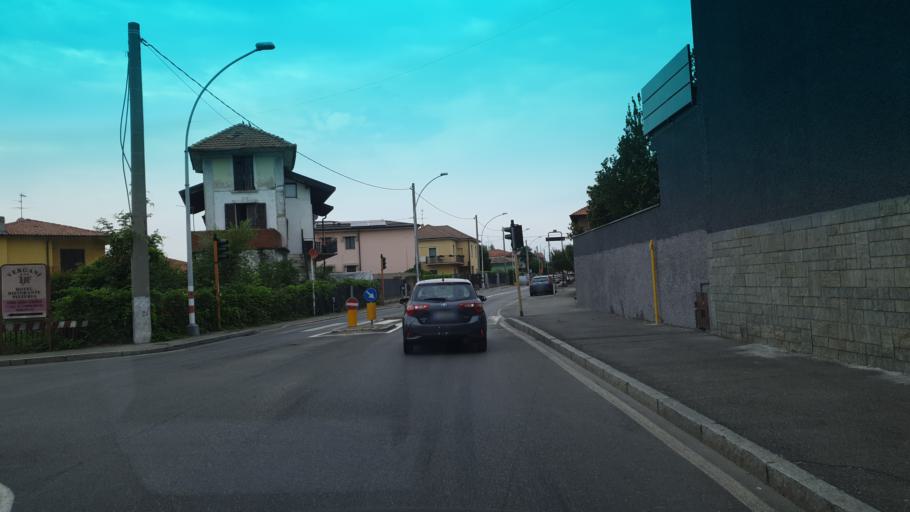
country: IT
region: Lombardy
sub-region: Provincia di Bergamo
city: Fara Gera d'Adda
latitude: 45.5503
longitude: 9.5348
